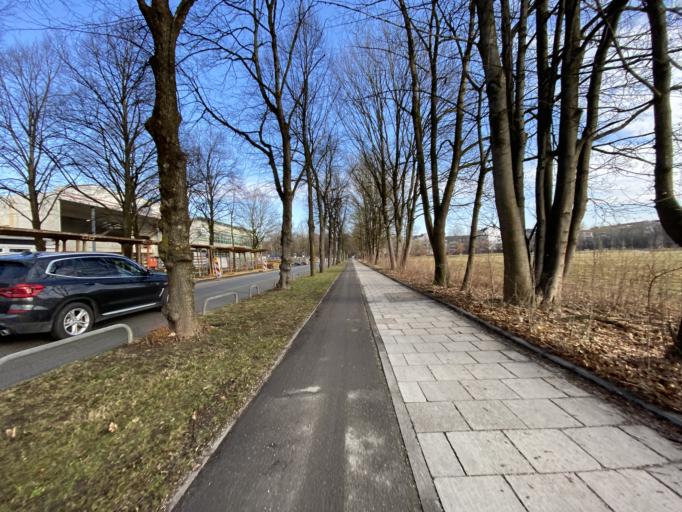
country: DE
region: Bavaria
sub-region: Upper Bavaria
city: Bogenhausen
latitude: 48.1449
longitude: 11.6280
